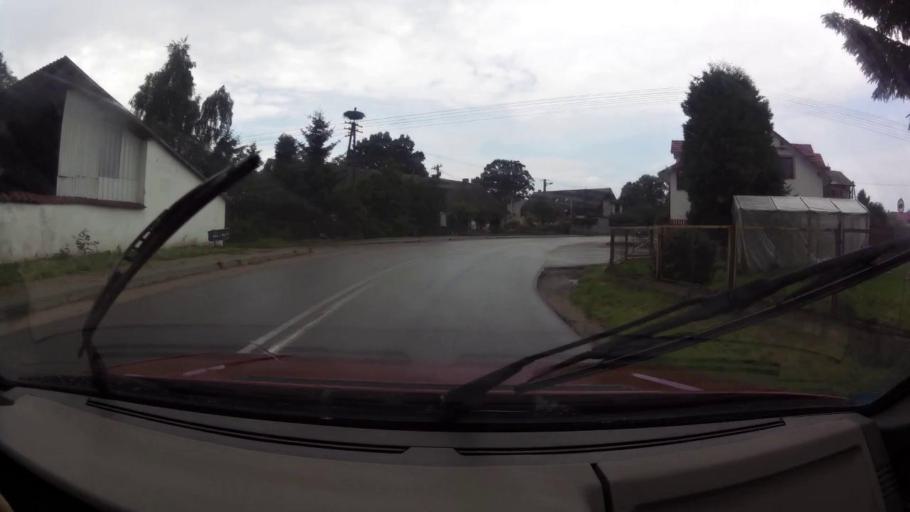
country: PL
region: West Pomeranian Voivodeship
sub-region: Koszalin
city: Koszalin
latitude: 54.1355
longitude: 16.1162
